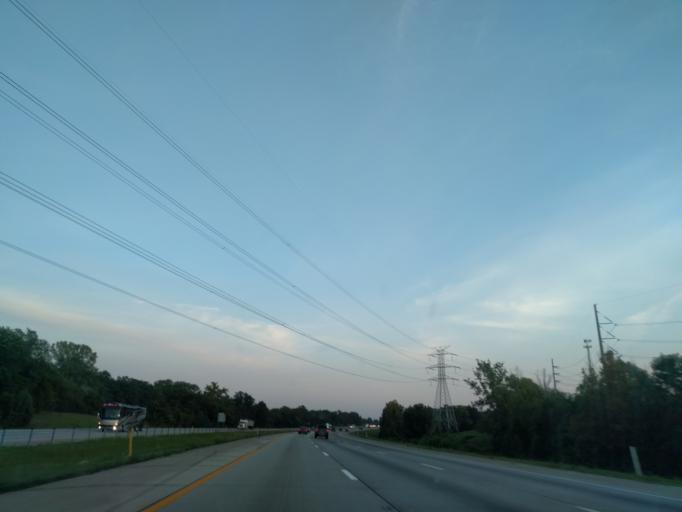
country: US
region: Kentucky
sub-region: Bullitt County
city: Brooks
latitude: 38.0447
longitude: -85.6973
